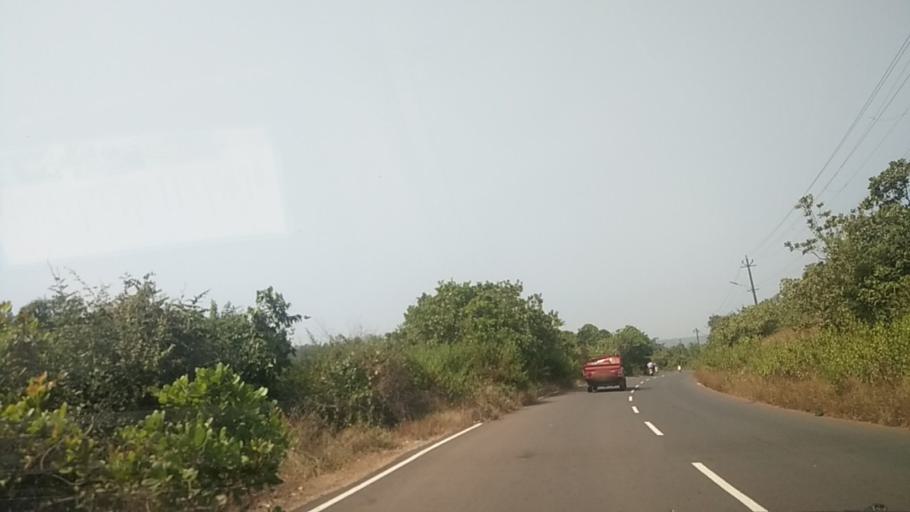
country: IN
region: Goa
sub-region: North Goa
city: Morjim
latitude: 15.6526
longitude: 73.7559
